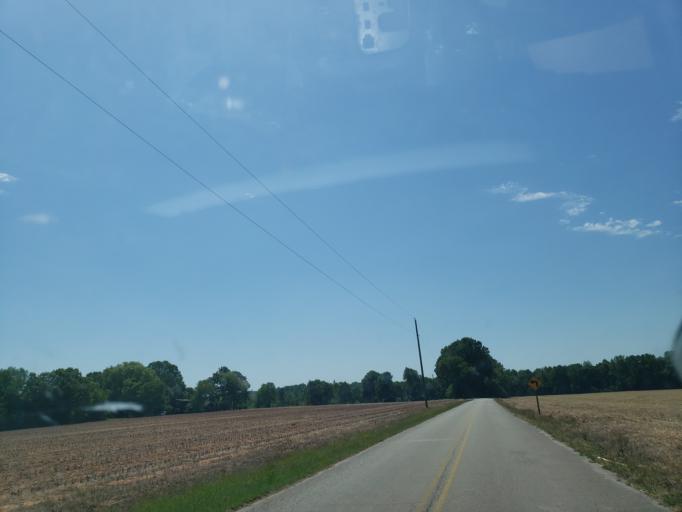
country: US
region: Alabama
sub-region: Madison County
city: Hazel Green
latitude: 34.9455
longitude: -86.5355
